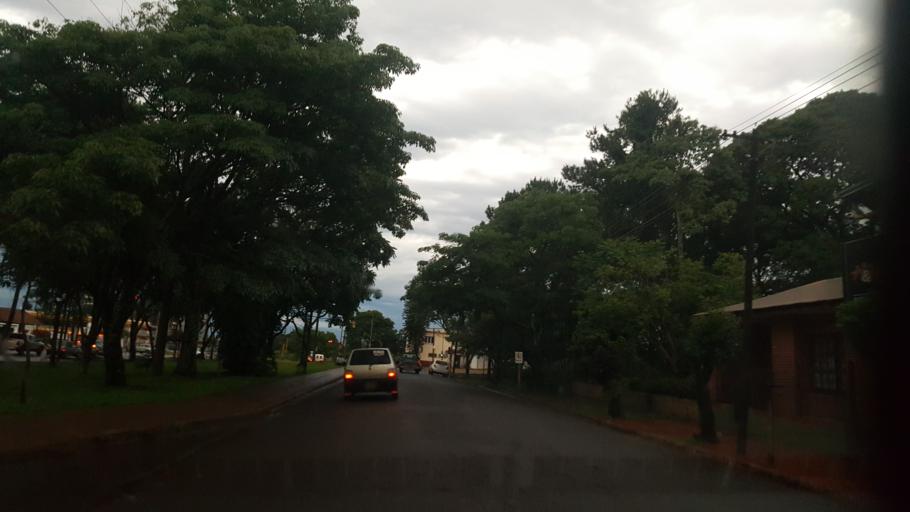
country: AR
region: Misiones
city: Jardin America
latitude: -27.0441
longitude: -55.2361
